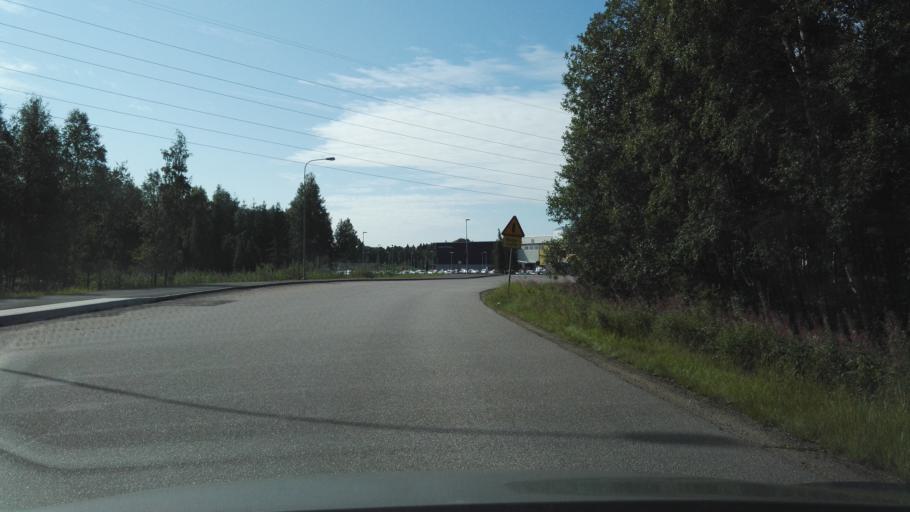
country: SE
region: Kronoberg
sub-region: Vaxjo Kommun
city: Vaexjoe
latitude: 56.8792
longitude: 14.7459
